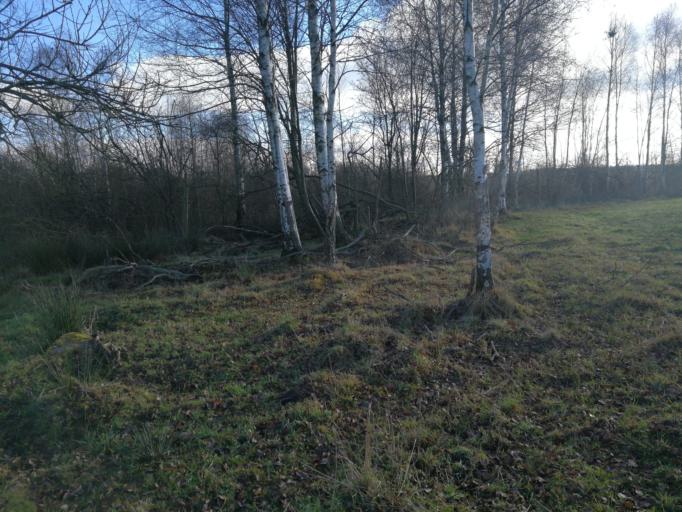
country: PL
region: Warmian-Masurian Voivodeship
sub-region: Powiat dzialdowski
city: Rybno
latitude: 53.4141
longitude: 19.9145
